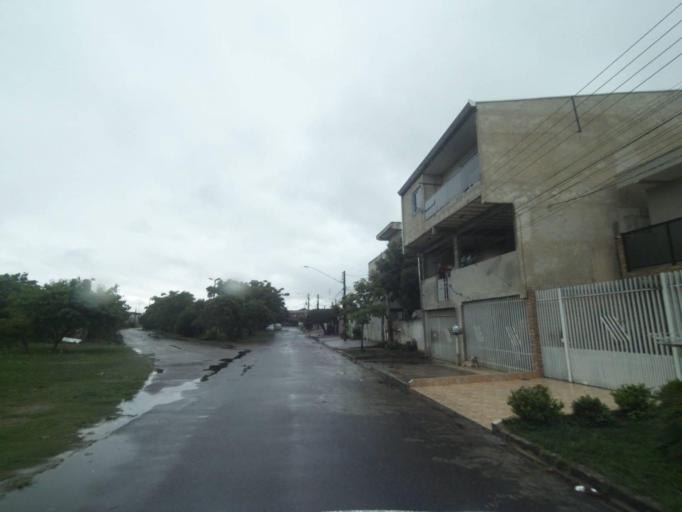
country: BR
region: Parana
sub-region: Araucaria
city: Araucaria
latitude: -25.5313
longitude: -49.3422
